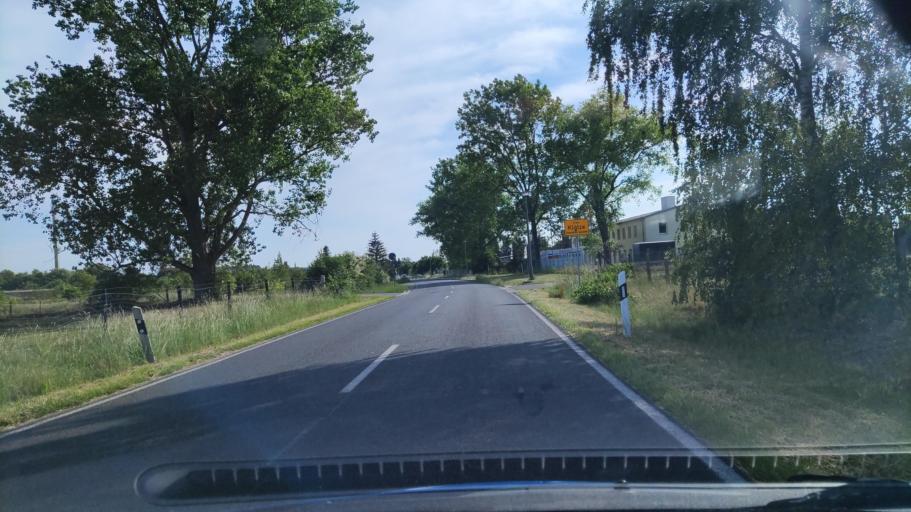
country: DE
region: Saxony-Anhalt
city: Klotze
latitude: 52.6363
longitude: 11.1764
